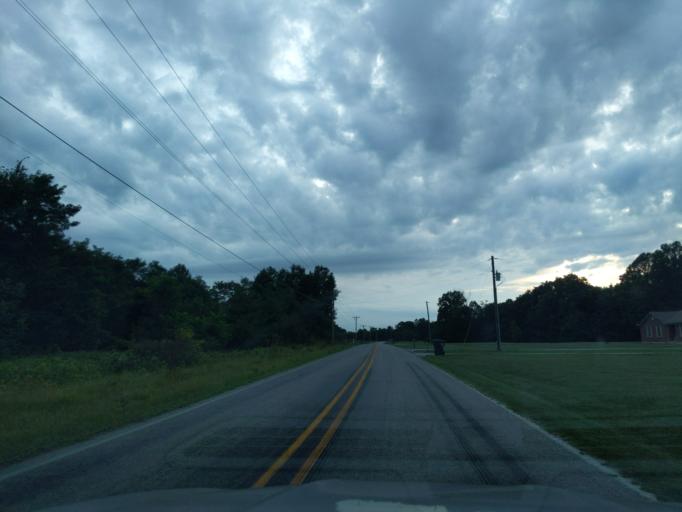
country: US
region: Indiana
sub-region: Ripley County
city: Osgood
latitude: 39.1953
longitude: -85.2665
